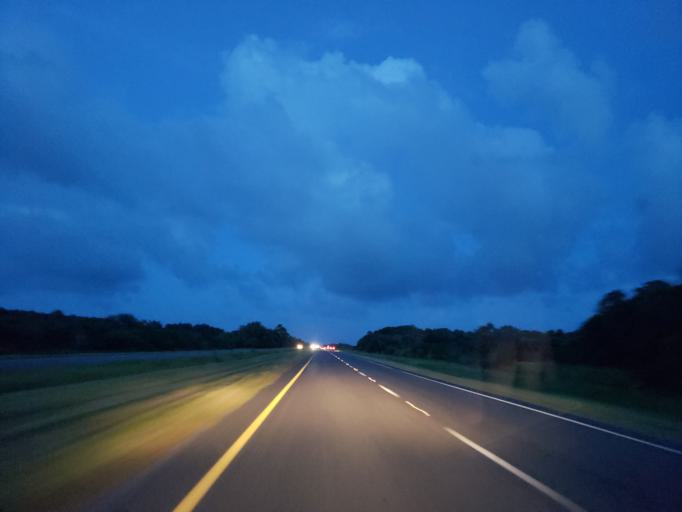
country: US
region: Florida
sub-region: Brevard County
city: June Park
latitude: 28.0916
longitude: -80.8599
